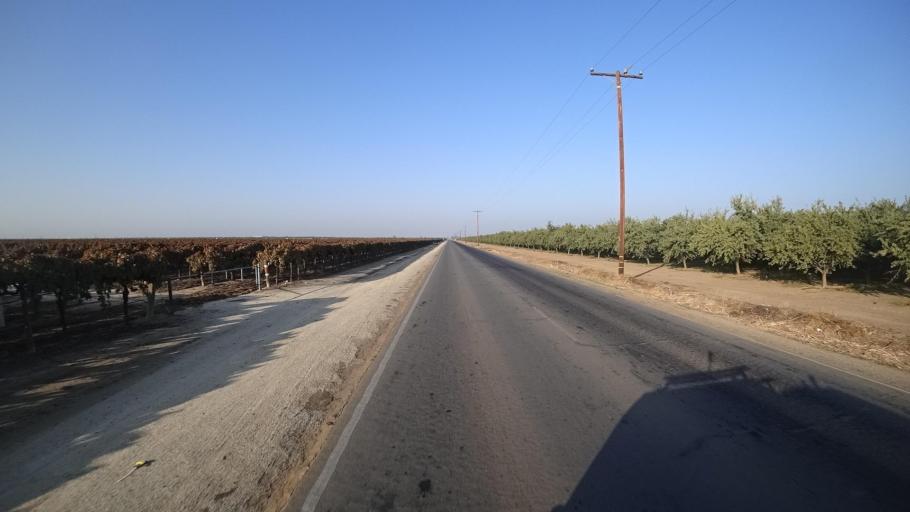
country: US
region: California
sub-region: Kern County
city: Delano
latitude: 35.7905
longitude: -119.1988
